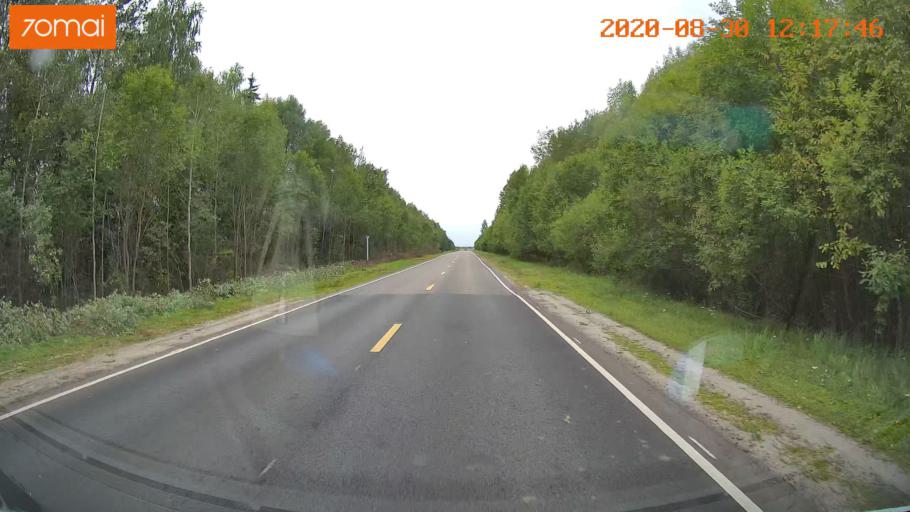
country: RU
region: Ivanovo
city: Yur'yevets
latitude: 57.3237
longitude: 42.9694
